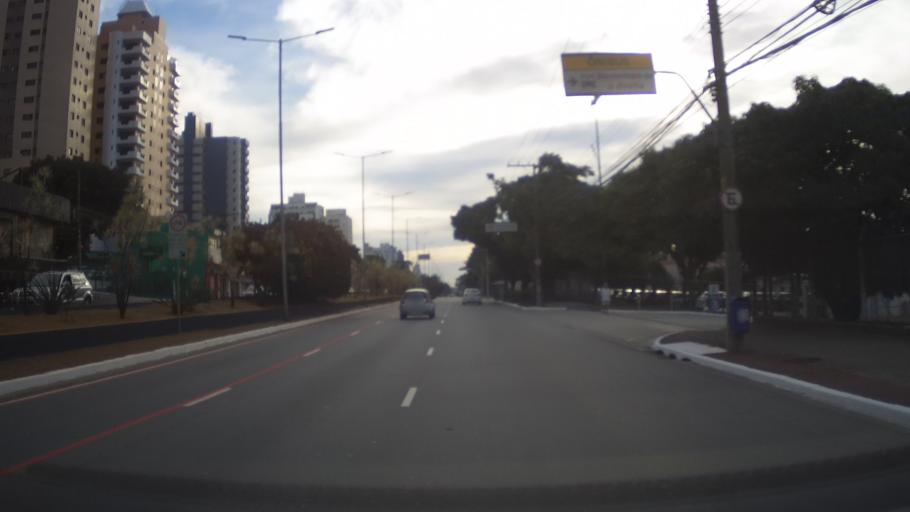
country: BR
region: Sao Paulo
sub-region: Sao Caetano Do Sul
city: Sao Caetano do Sul
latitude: -23.6164
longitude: -46.5609
